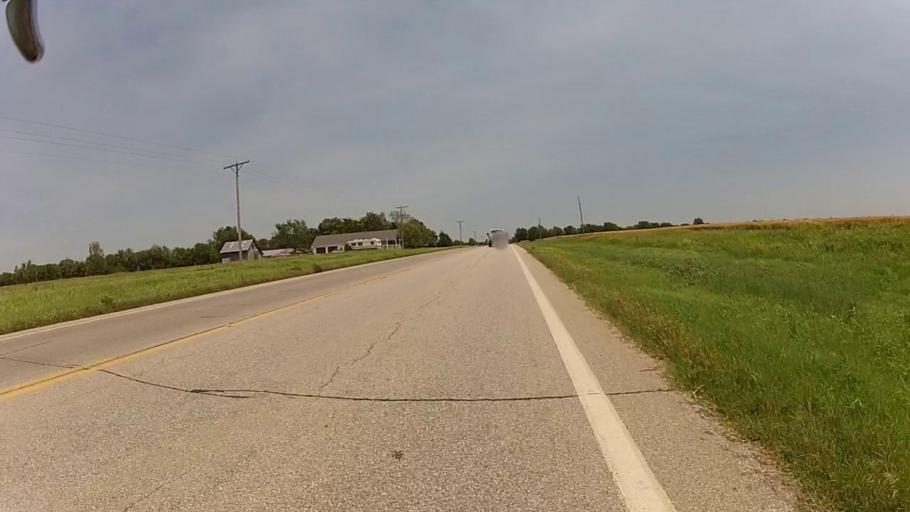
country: US
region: Kansas
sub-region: Cowley County
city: Arkansas City
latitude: 37.0563
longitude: -97.0867
